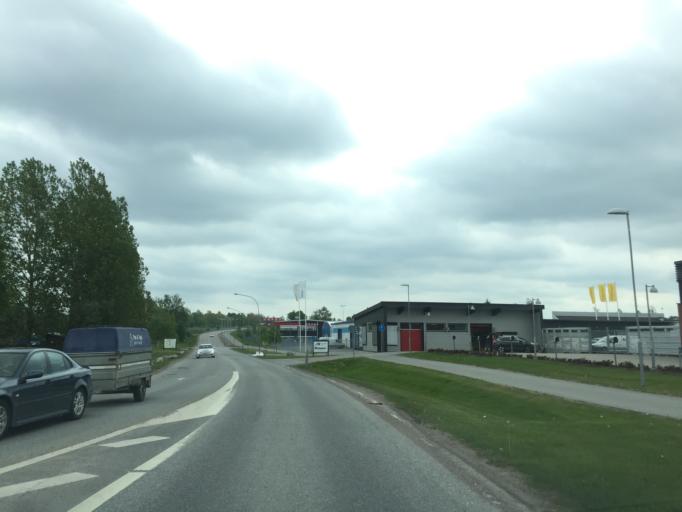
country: SE
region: OErebro
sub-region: Orebro Kommun
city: Orebro
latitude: 59.2578
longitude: 15.1776
